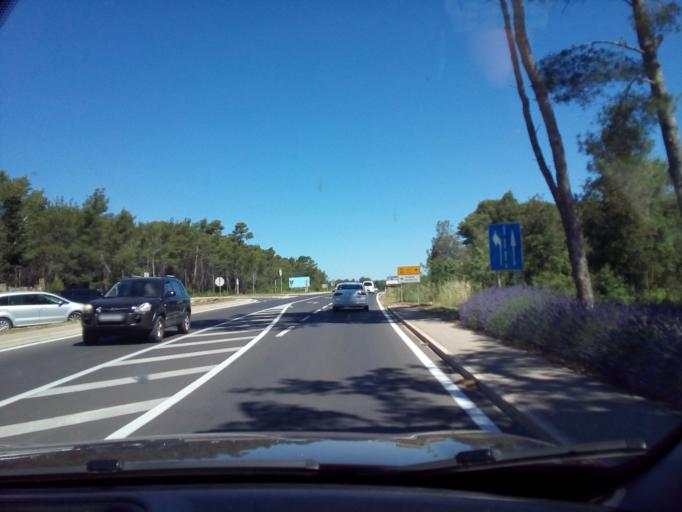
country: HR
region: Zadarska
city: Nin
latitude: 44.1754
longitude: 15.1907
